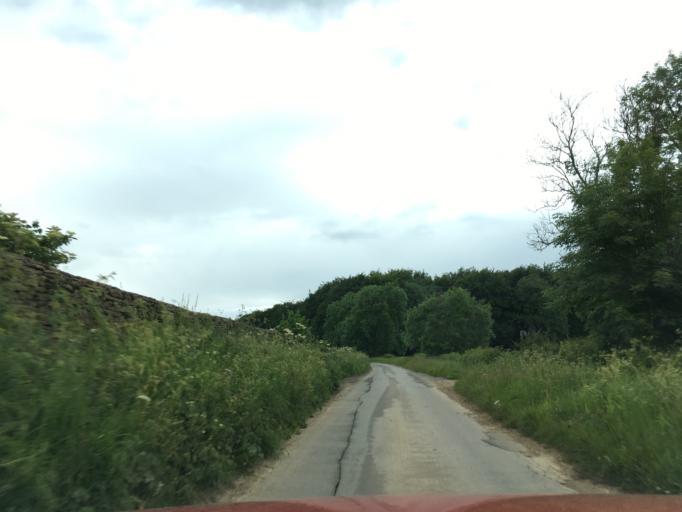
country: GB
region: England
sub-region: Wiltshire
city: Luckington
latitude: 51.5721
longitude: -2.2674
